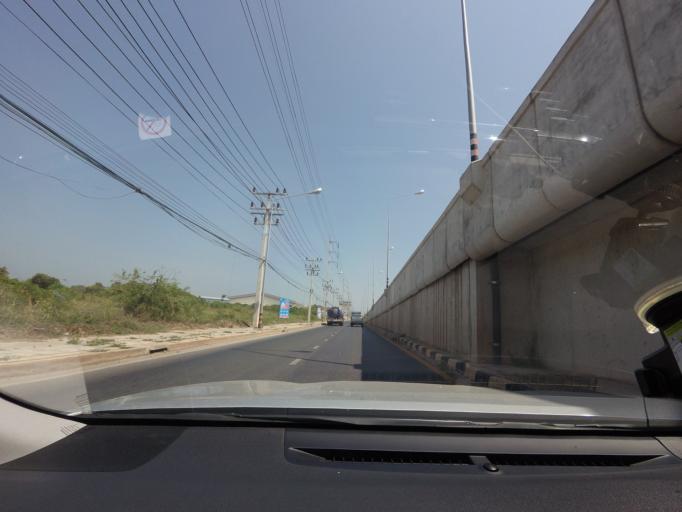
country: TH
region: Surat Thani
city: Surat Thani
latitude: 9.1553
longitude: 99.3698
